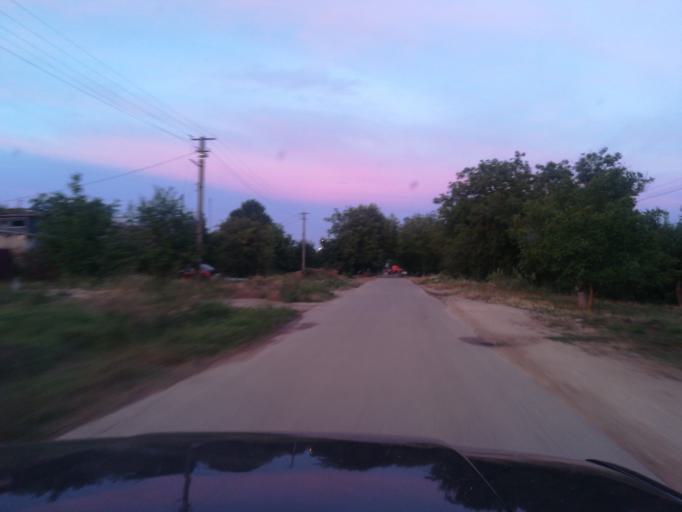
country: RU
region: Krasnodarskiy
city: Yurovka
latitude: 45.1142
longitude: 37.4324
